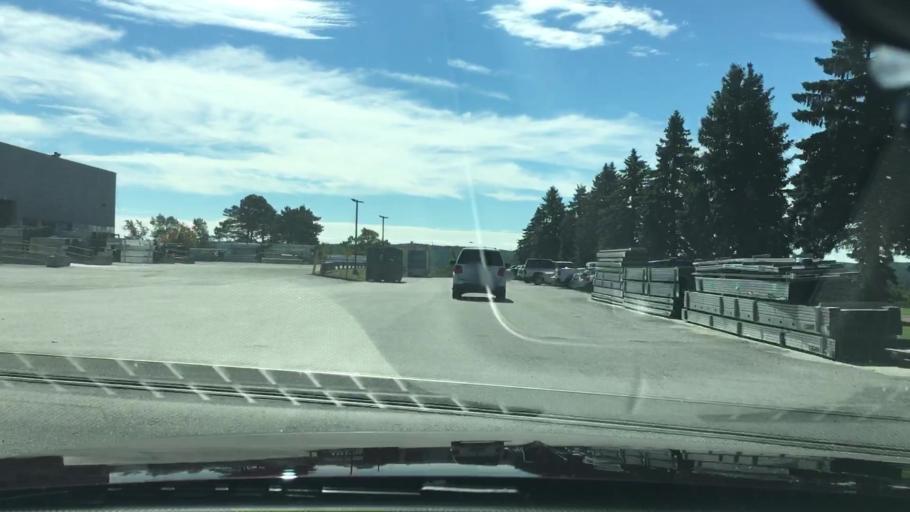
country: US
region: Connecticut
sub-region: Litchfield County
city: Terryville
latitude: 41.6942
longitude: -72.9820
